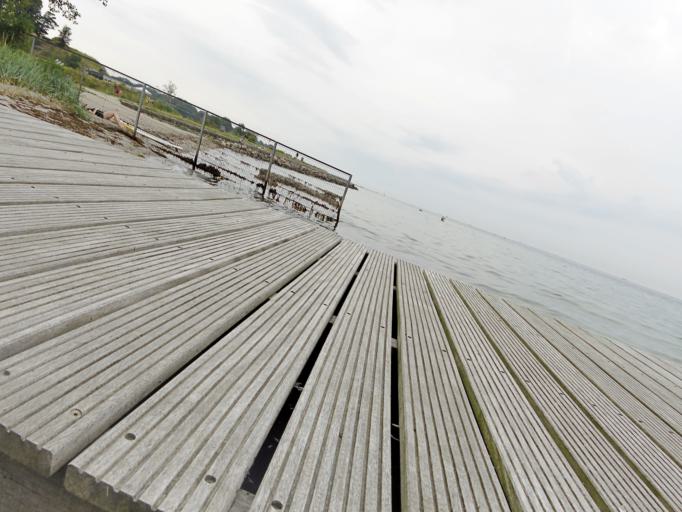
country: DK
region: Capital Region
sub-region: Gentofte Kommune
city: Charlottenlund
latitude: 55.7436
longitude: 12.5878
